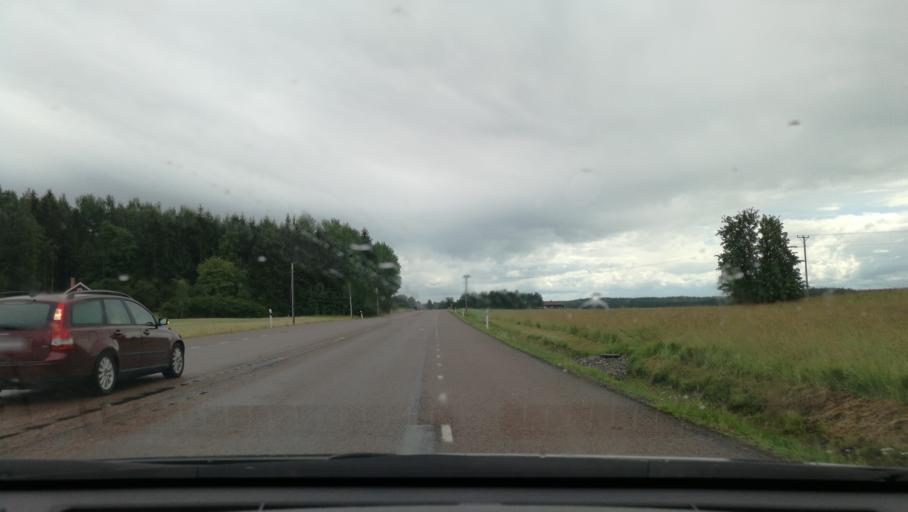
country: SE
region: Vaestmanland
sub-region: Kopings Kommun
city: Koping
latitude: 59.4745
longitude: 15.9906
